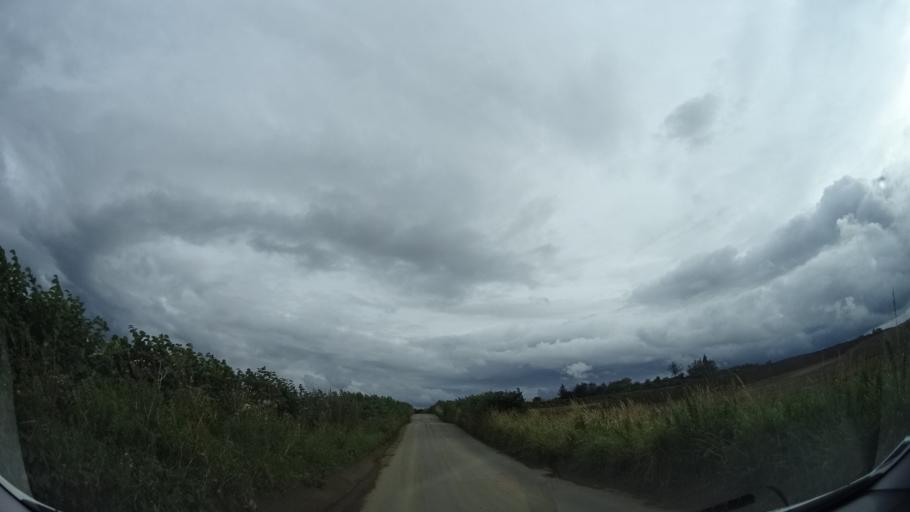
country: GB
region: Scotland
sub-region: West Lothian
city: Kirknewton
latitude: 55.9028
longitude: -3.4344
